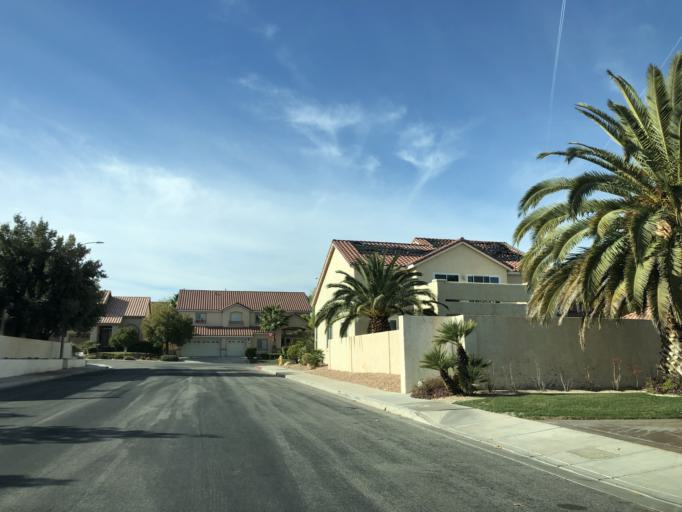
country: US
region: Nevada
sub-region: Clark County
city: Whitney
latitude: 36.0143
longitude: -115.0794
